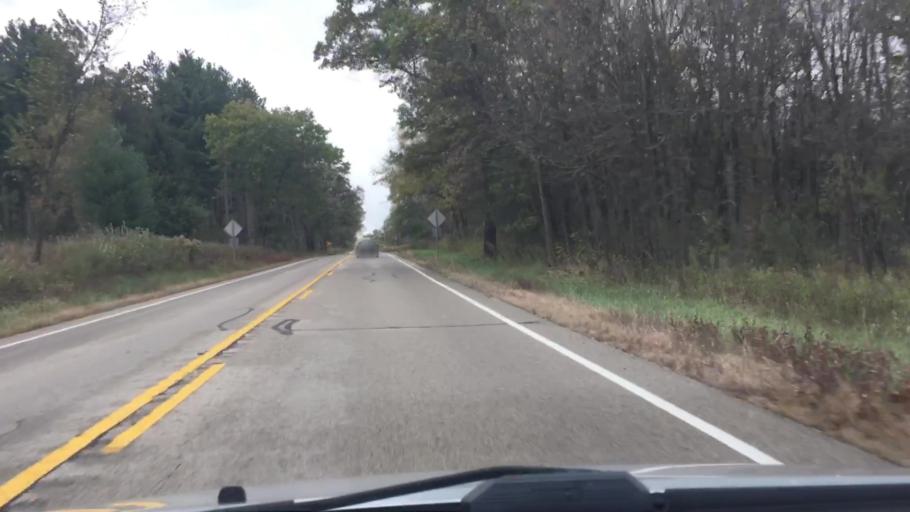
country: US
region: Wisconsin
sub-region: Waukesha County
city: Eagle
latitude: 42.9158
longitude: -88.4738
